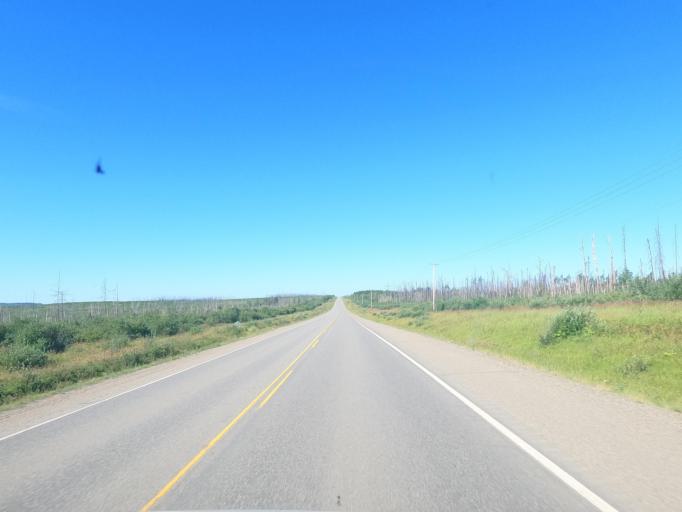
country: CA
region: British Columbia
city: Fort St. John
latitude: 56.5517
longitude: -121.2746
